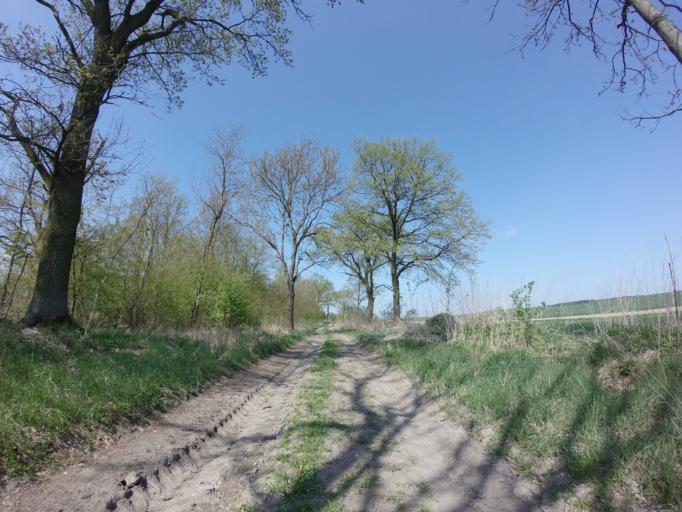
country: PL
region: West Pomeranian Voivodeship
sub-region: Powiat choszczenski
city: Choszczno
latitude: 53.2053
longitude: 15.3640
